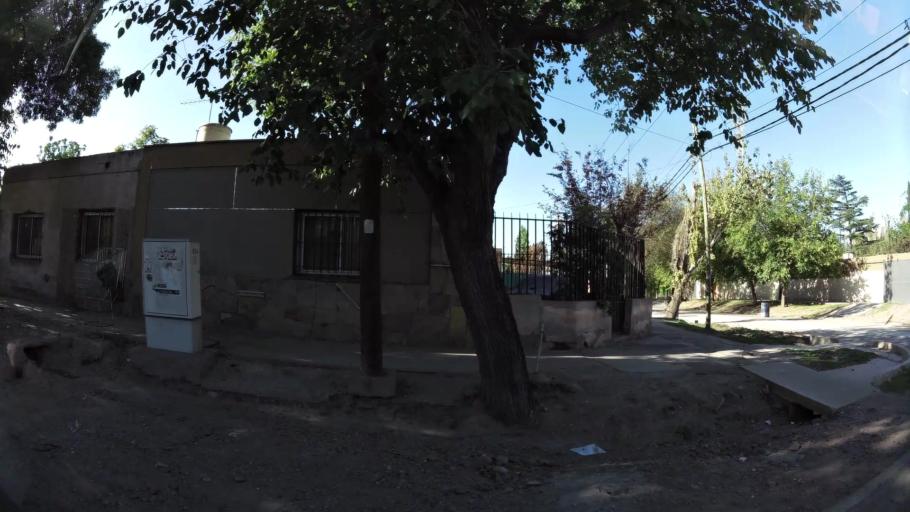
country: AR
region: Mendoza
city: Mendoza
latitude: -32.9018
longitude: -68.8049
